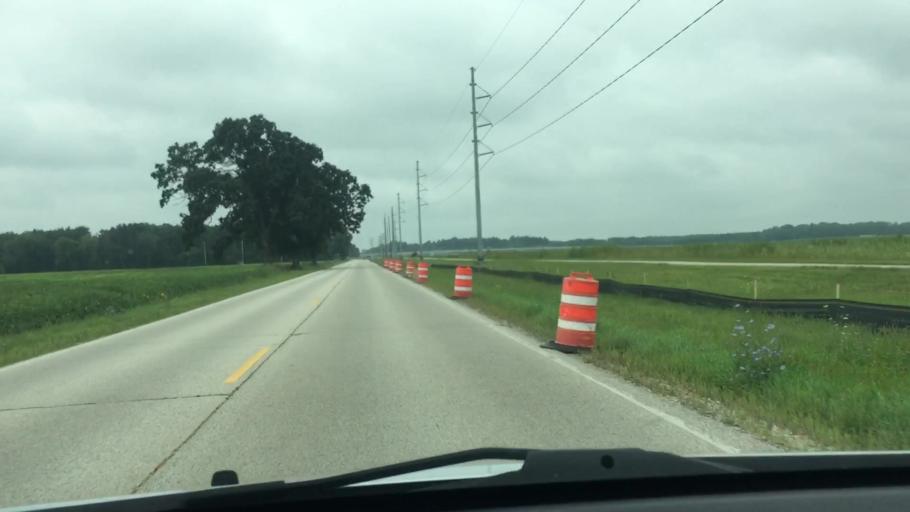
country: US
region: Wisconsin
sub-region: Waukesha County
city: Delafield
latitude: 43.0731
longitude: -88.4420
